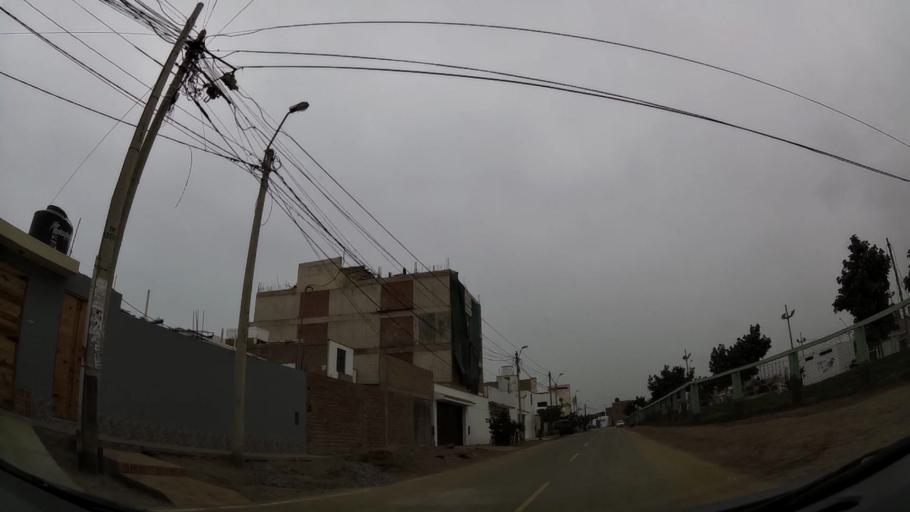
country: PE
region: Lima
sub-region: Lima
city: Punta Hermosa
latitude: -12.3172
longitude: -76.8334
